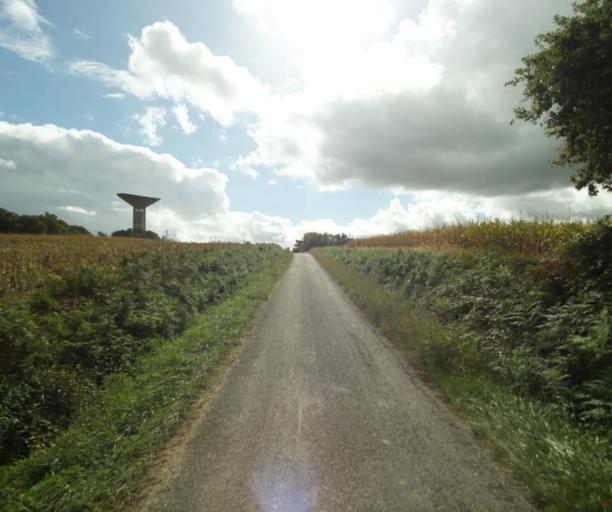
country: FR
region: Midi-Pyrenees
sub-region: Departement du Gers
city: Eauze
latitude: 43.8636
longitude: 0.0694
